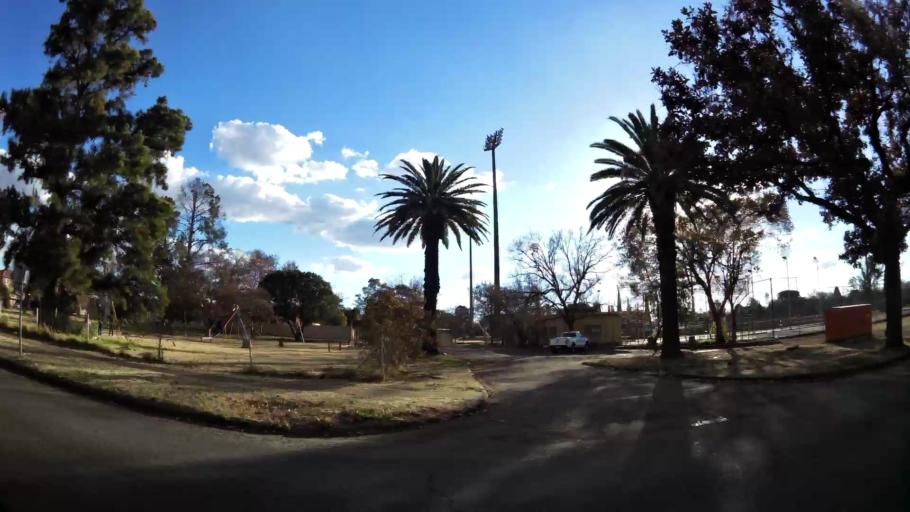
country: ZA
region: North-West
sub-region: Dr Kenneth Kaunda District Municipality
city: Potchefstroom
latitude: -26.7122
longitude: 27.0911
